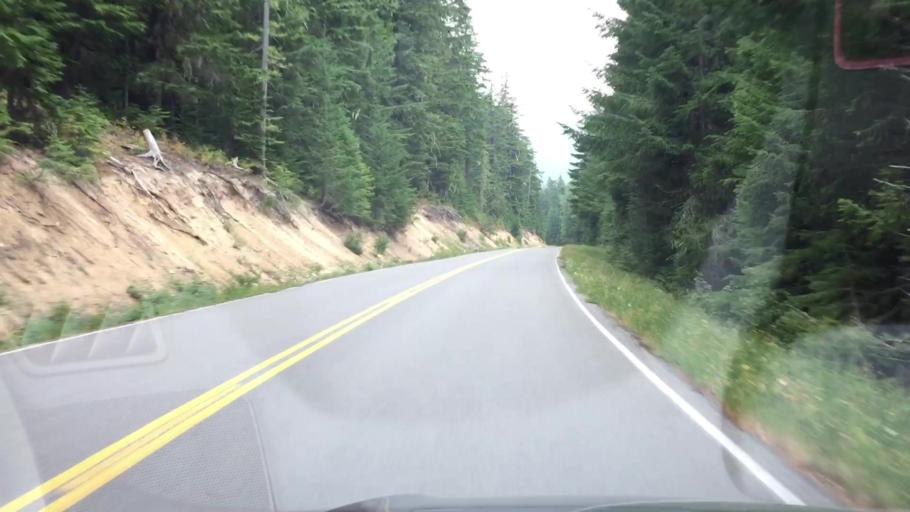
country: US
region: Washington
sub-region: Klickitat County
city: White Salmon
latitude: 46.1187
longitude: -121.6205
